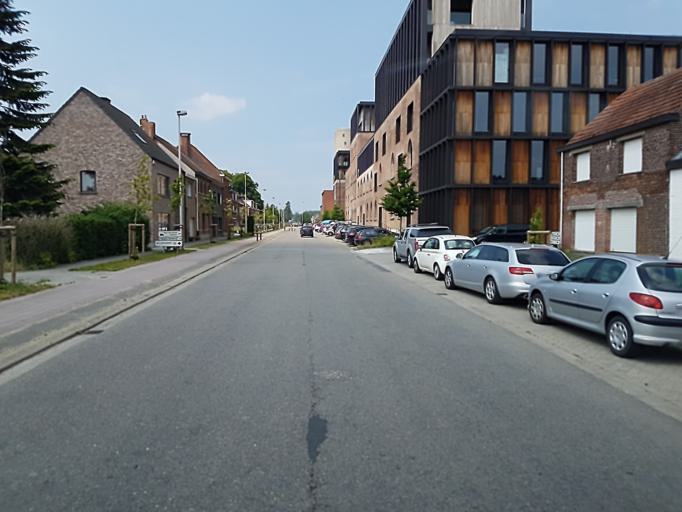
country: BE
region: Flanders
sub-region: Provincie Antwerpen
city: Wijnegem
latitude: 51.2221
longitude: 4.5450
